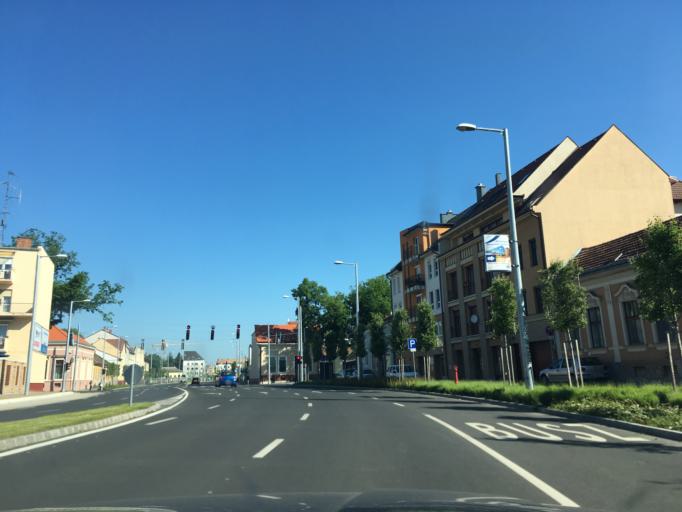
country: HU
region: Hajdu-Bihar
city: Debrecen
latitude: 47.5243
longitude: 21.6232
